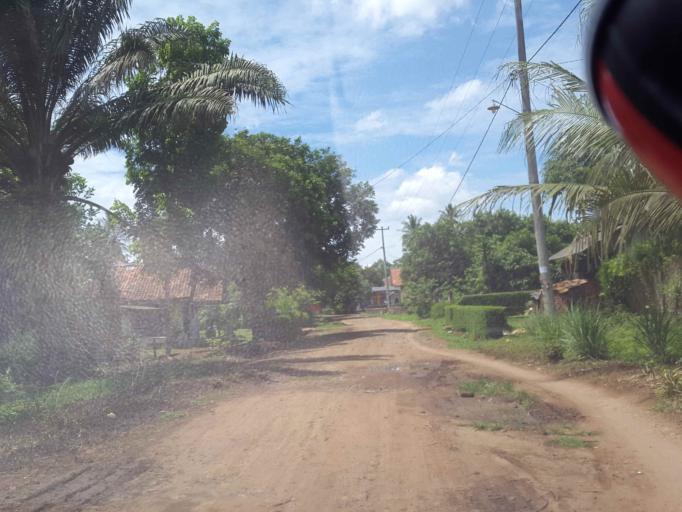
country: ID
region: Lampung
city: Natar
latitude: -5.3210
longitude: 105.1843
